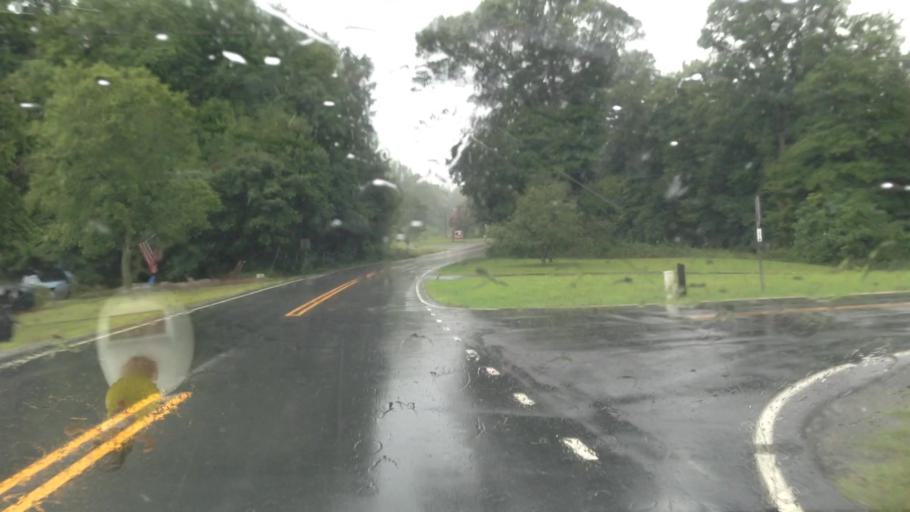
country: US
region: North Carolina
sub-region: Stokes County
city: Danbury
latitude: 36.4358
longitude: -80.1021
